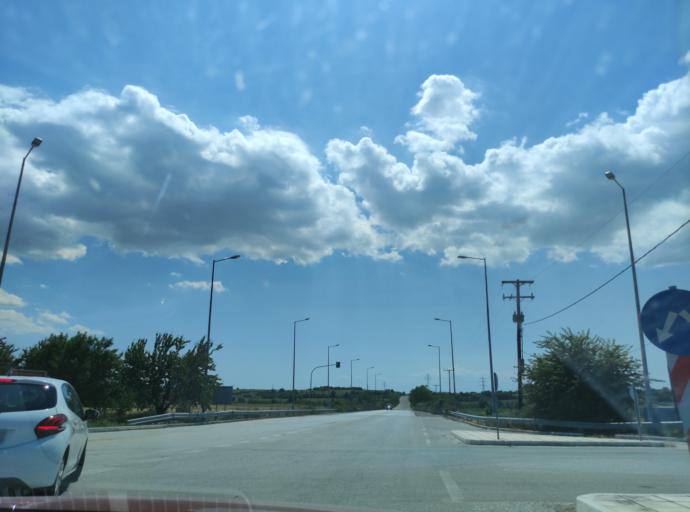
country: GR
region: Central Macedonia
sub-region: Nomos Serron
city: Proti
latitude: 40.9835
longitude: 24.0290
